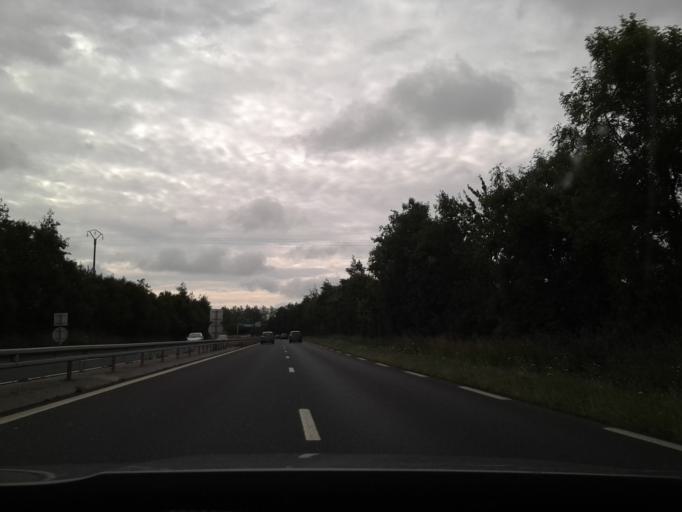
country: FR
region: Lower Normandy
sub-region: Departement de la Manche
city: Saint-Hilaire-Petitville
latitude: 49.3079
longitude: -1.2176
